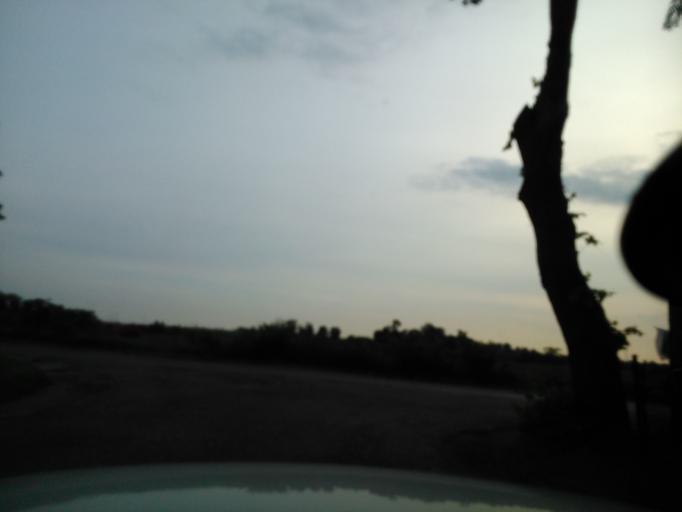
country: PL
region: Kujawsko-Pomorskie
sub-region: Powiat golubsko-dobrzynski
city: Kowalewo Pomorskie
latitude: 53.1216
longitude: 18.9135
